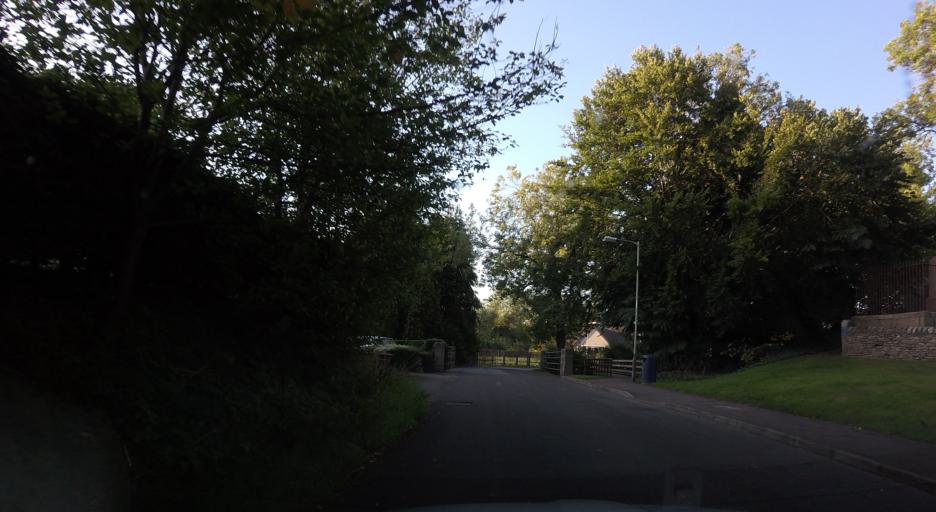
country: GB
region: Scotland
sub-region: Angus
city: Muirhead
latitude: 56.4587
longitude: -3.0557
